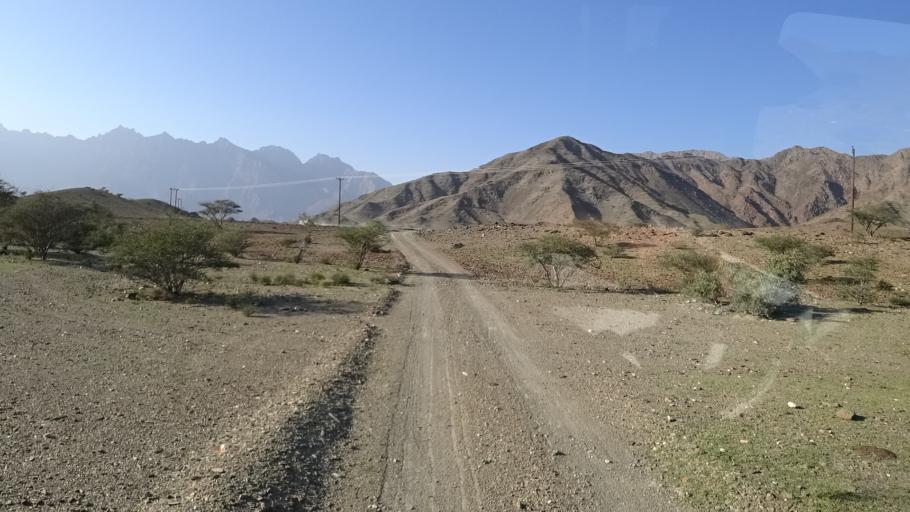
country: OM
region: Al Batinah
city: Rustaq
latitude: 23.2750
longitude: 57.3606
